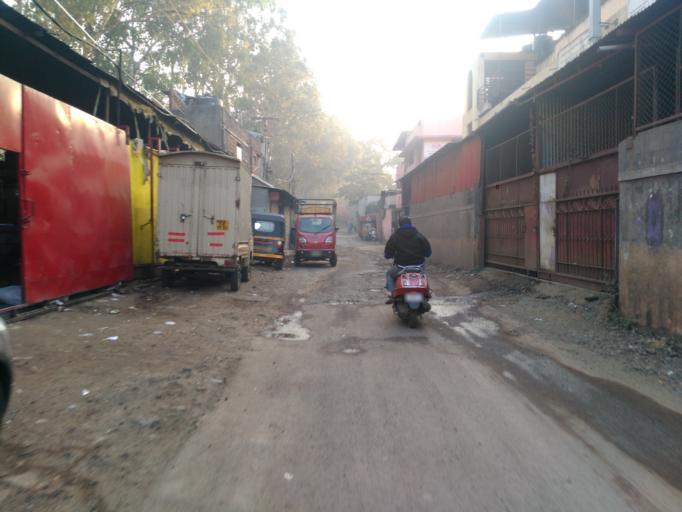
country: IN
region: Maharashtra
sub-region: Pune Division
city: Pune
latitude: 18.4455
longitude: 73.8946
